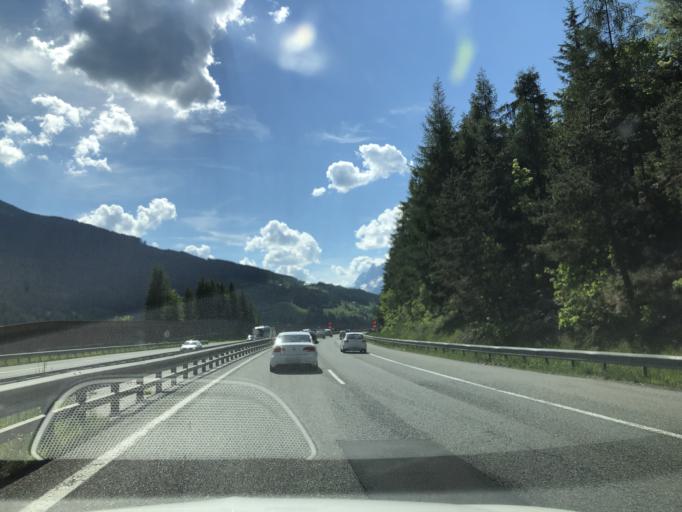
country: AT
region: Salzburg
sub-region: Politischer Bezirk Sankt Johann im Pongau
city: Huttau
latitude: 47.4192
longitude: 13.3157
